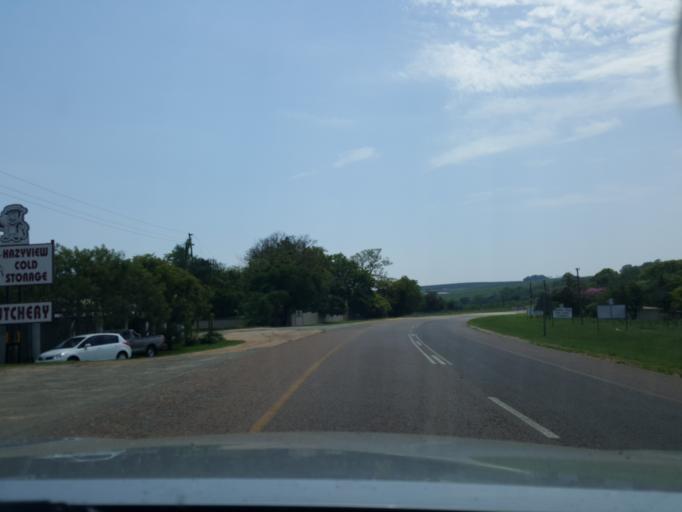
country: ZA
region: Mpumalanga
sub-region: Ehlanzeni District
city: White River
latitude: -25.0794
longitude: 31.0830
